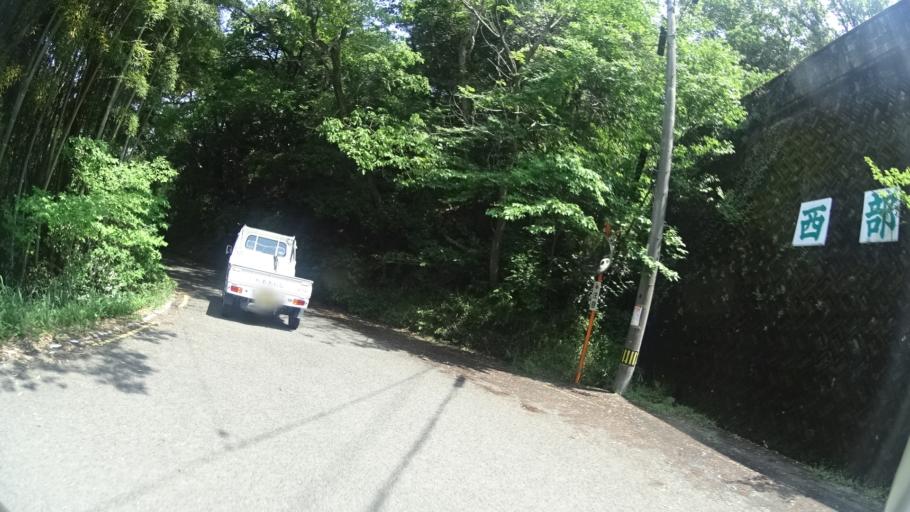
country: JP
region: Tokushima
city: Tokushima-shi
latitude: 34.0701
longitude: 134.5130
